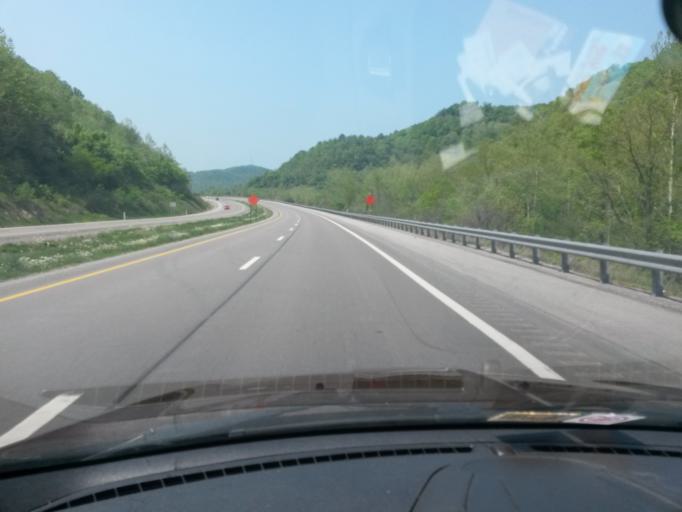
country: US
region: West Virginia
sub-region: Gilmer County
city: Glenville
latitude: 38.8707
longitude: -80.6422
